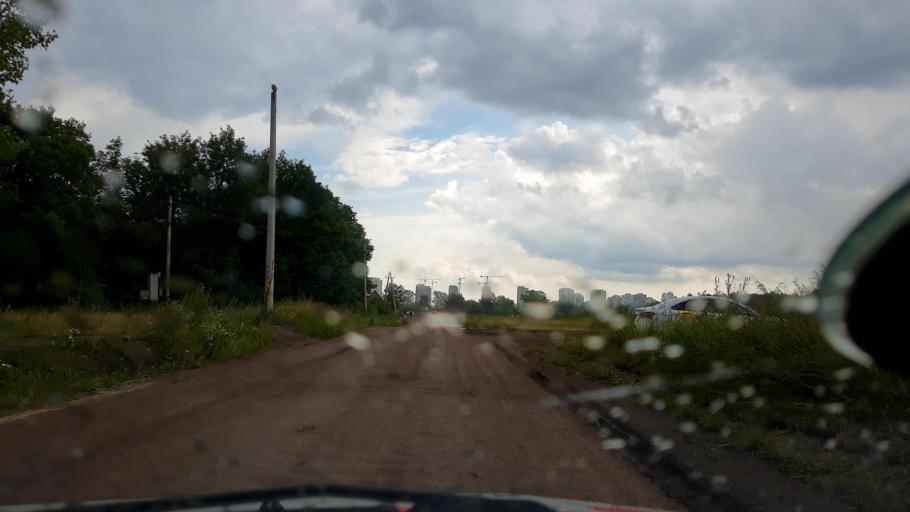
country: RU
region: Bashkortostan
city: Mikhaylovka
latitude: 54.7117
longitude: 55.8683
